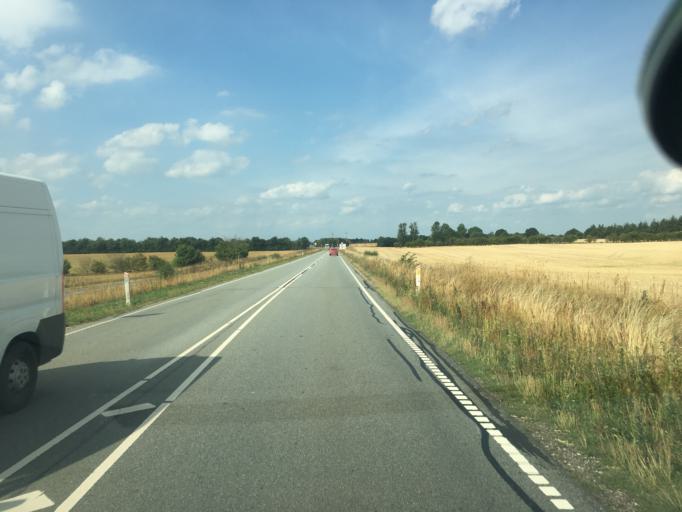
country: DK
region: South Denmark
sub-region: Aabenraa Kommune
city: Krusa
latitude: 54.9394
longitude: 9.3717
